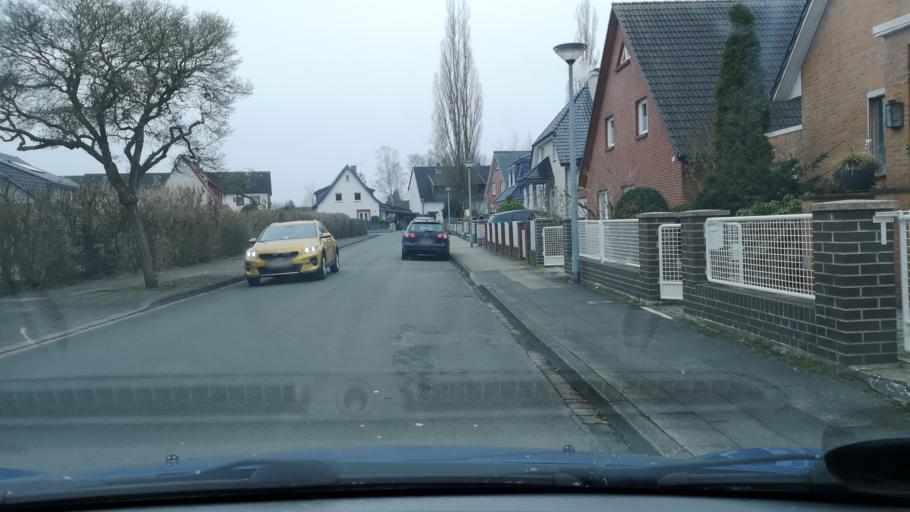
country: DE
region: Lower Saxony
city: Celle
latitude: 52.6053
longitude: 10.0597
